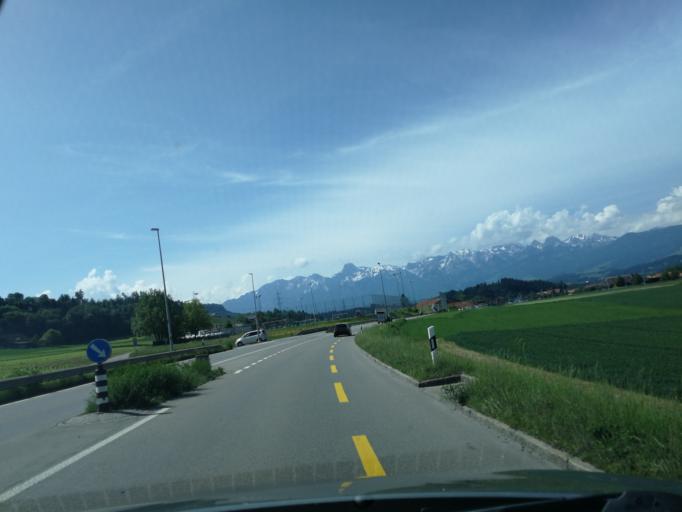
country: CH
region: Lucerne
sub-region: Entlebuch District
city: Oberdiessbach
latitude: 46.8348
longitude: 7.6176
